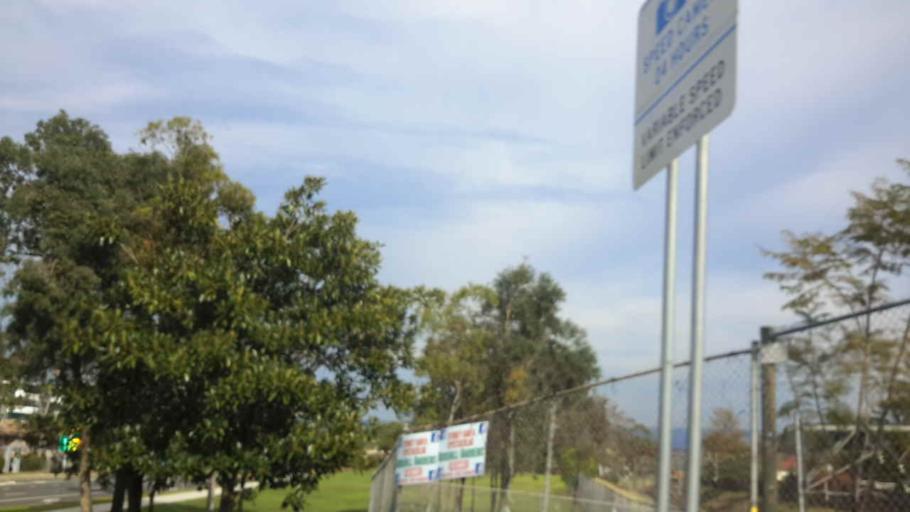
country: AU
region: New South Wales
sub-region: Penrith Municipality
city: Kingswood Park
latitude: -33.7566
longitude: 150.7121
